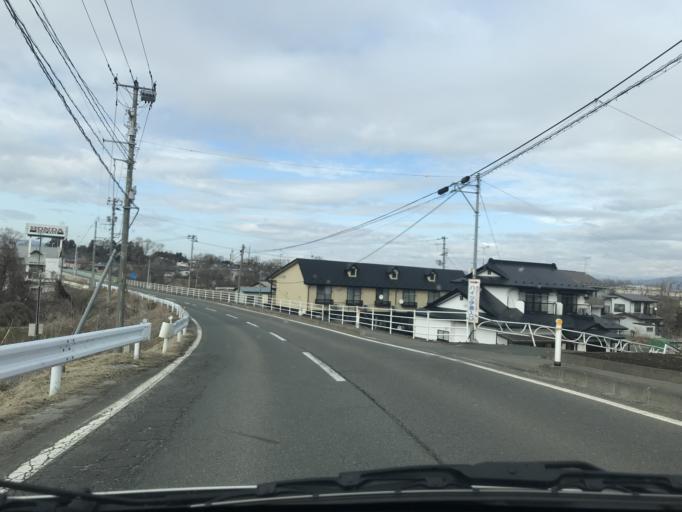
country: JP
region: Iwate
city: Hanamaki
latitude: 39.3769
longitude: 141.1067
